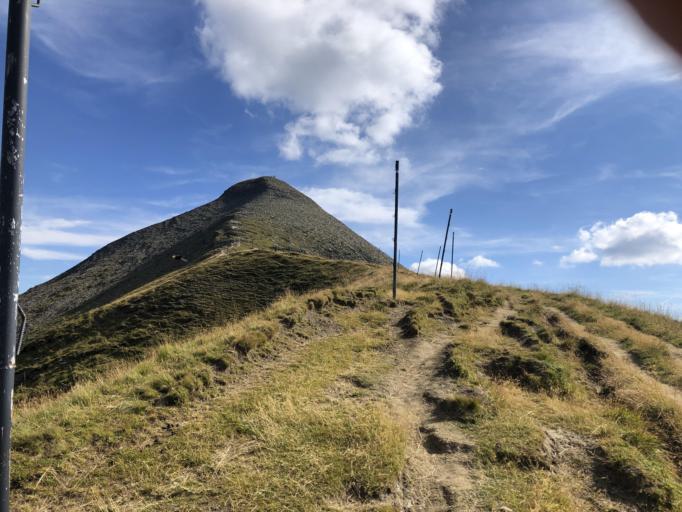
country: FR
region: Rhone-Alpes
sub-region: Departement de la Haute-Savoie
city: Les Contamines-Montjoie
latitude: 45.8318
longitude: 6.6924
